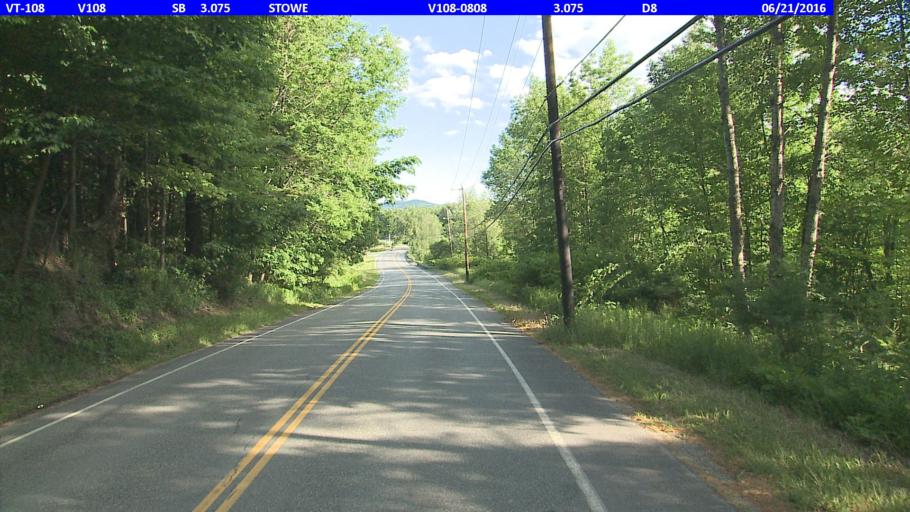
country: US
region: Vermont
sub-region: Lamoille County
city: Morristown
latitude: 44.4854
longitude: -72.7283
